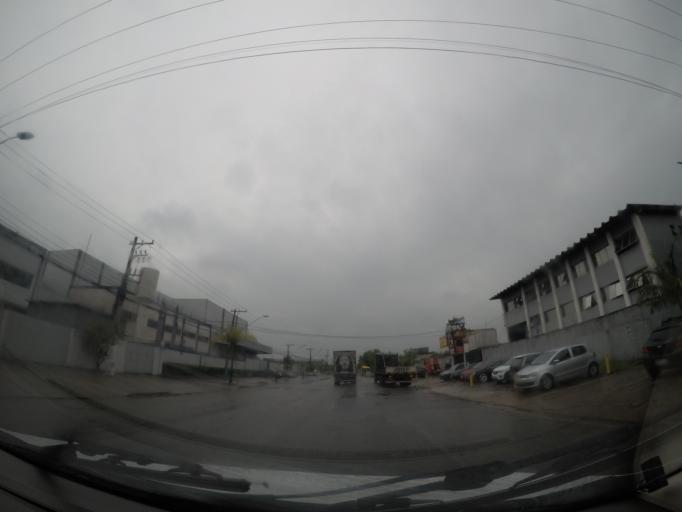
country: BR
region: Sao Paulo
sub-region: Guarulhos
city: Guarulhos
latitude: -23.4737
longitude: -46.4761
